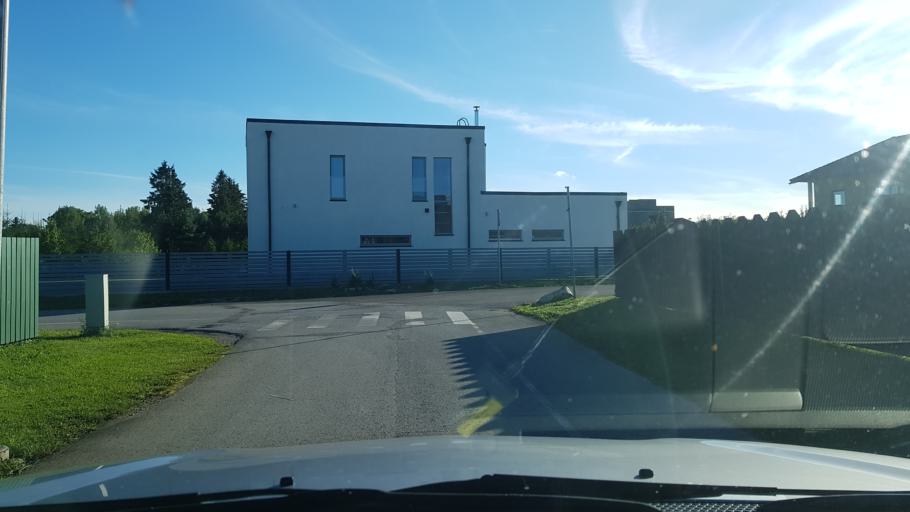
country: EE
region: Harju
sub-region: Rae vald
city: Jueri
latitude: 59.3841
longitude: 24.8469
